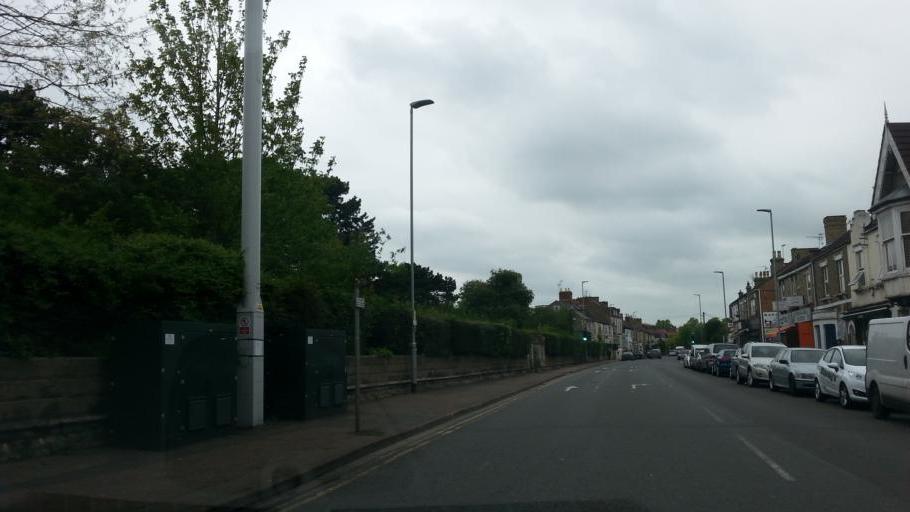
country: GB
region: England
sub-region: Peterborough
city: Peterborough
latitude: 52.5789
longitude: -0.2342
